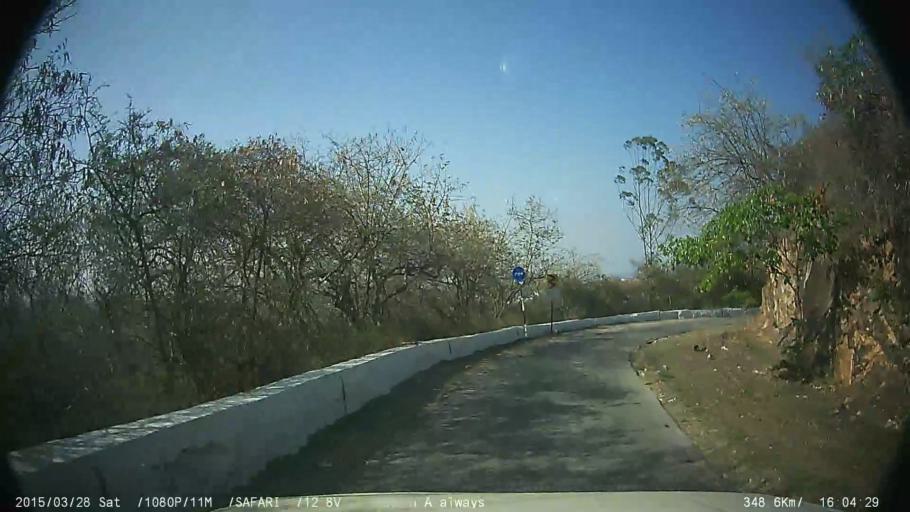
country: IN
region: Karnataka
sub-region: Mysore
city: Mysore
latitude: 12.2816
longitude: 76.6756
